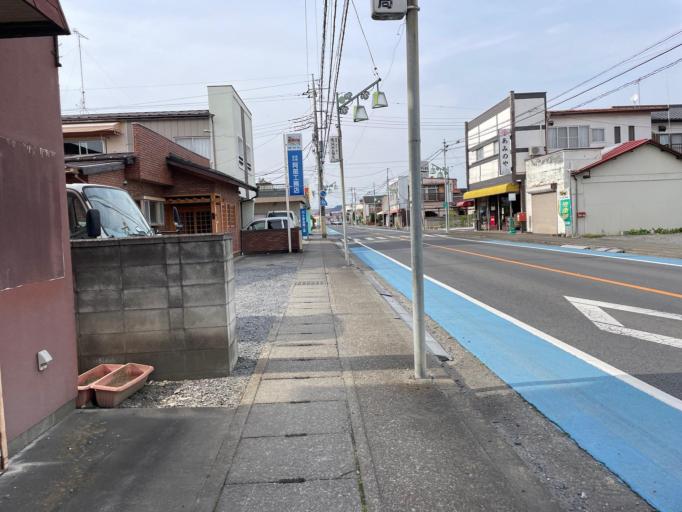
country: JP
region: Tochigi
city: Mibu
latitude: 36.4217
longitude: 139.8022
